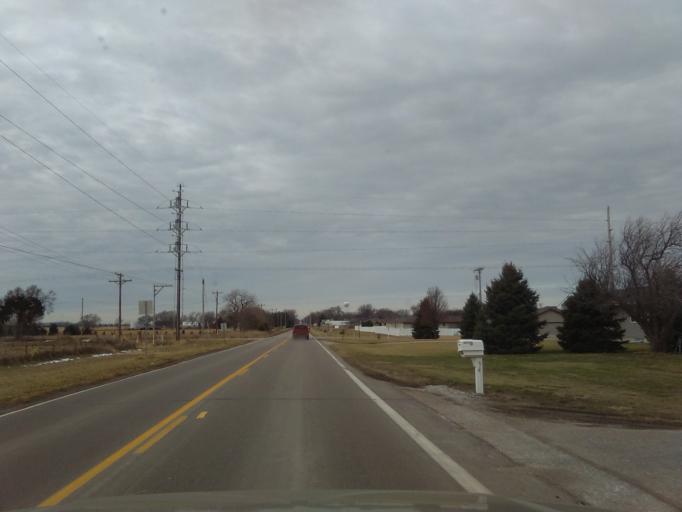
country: US
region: Nebraska
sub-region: Hall County
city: Grand Island
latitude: 40.7710
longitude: -98.3581
